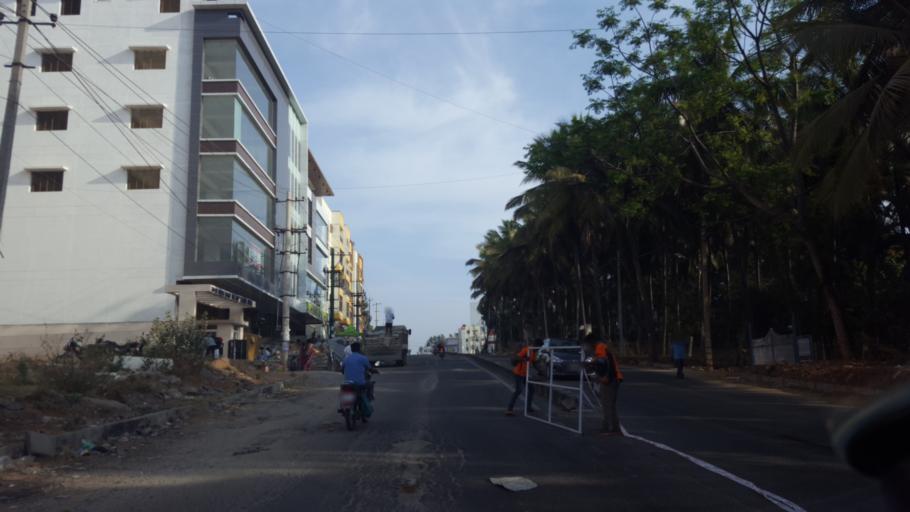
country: IN
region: Karnataka
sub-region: Bangalore Urban
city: Bangalore
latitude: 12.9109
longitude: 77.5136
